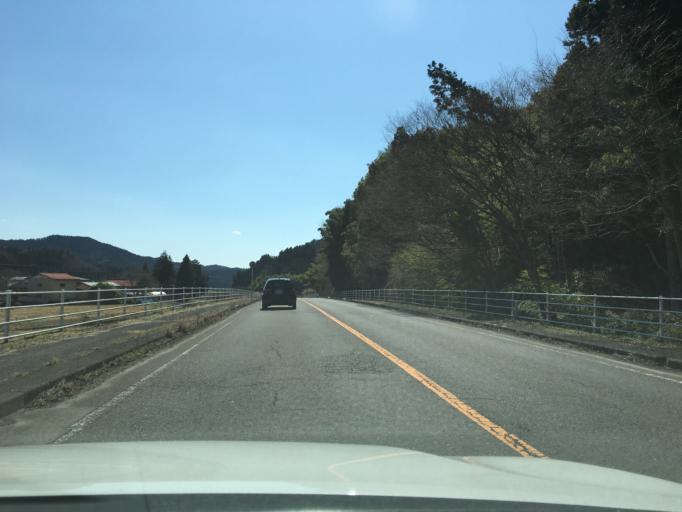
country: JP
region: Tochigi
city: Kuroiso
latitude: 37.0187
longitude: 140.1781
